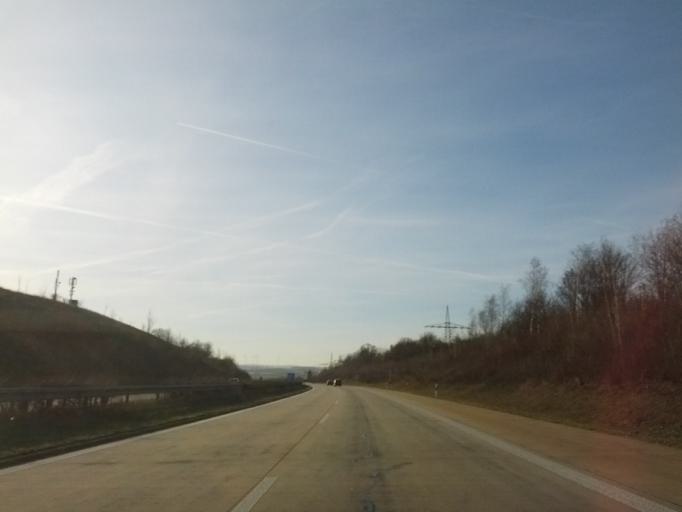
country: DE
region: Bavaria
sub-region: Regierungsbezirk Mittelfranken
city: Neusitz
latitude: 49.3861
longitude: 10.2263
